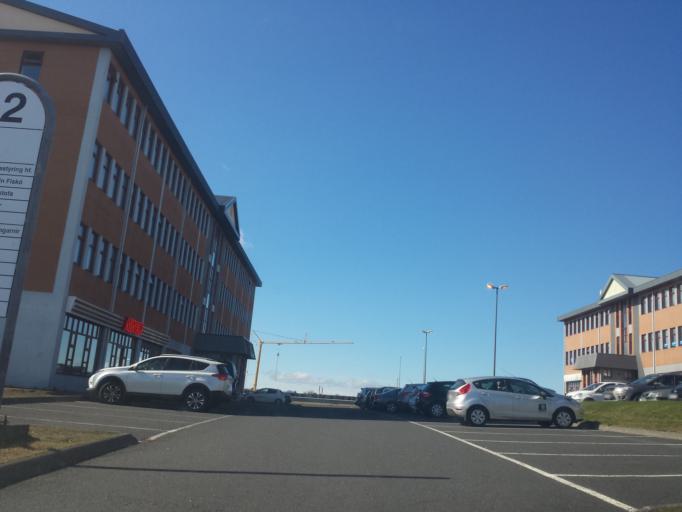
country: IS
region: Capital Region
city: Kopavogur
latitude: 64.0966
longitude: -21.8900
